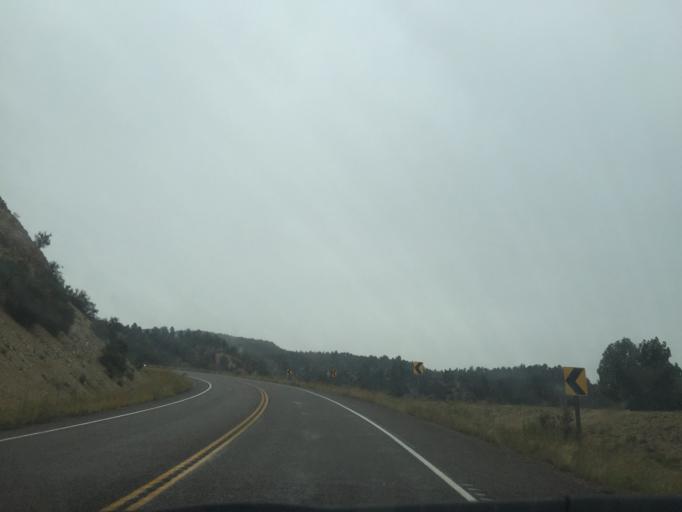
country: US
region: Utah
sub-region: Kane County
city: Kanab
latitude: 37.2054
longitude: -112.6854
